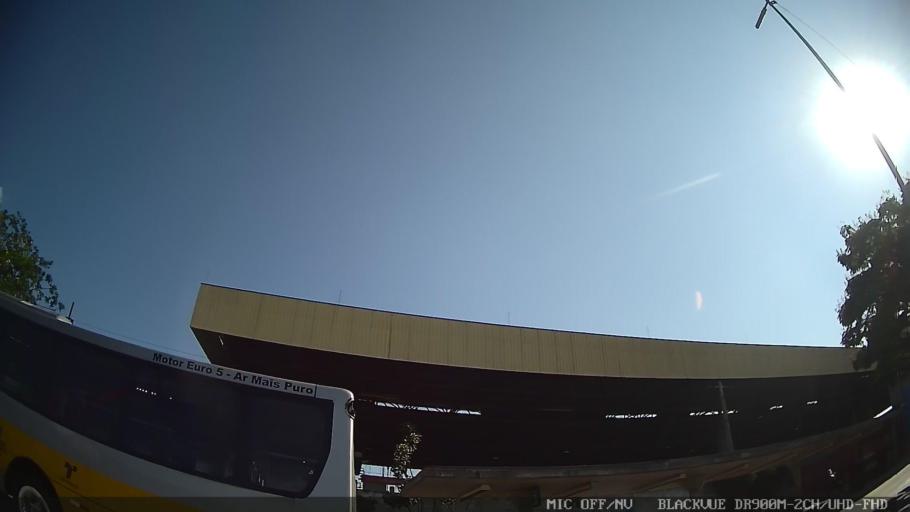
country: BR
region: Sao Paulo
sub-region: Ferraz De Vasconcelos
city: Ferraz de Vasconcelos
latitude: -23.5420
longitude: -46.4152
